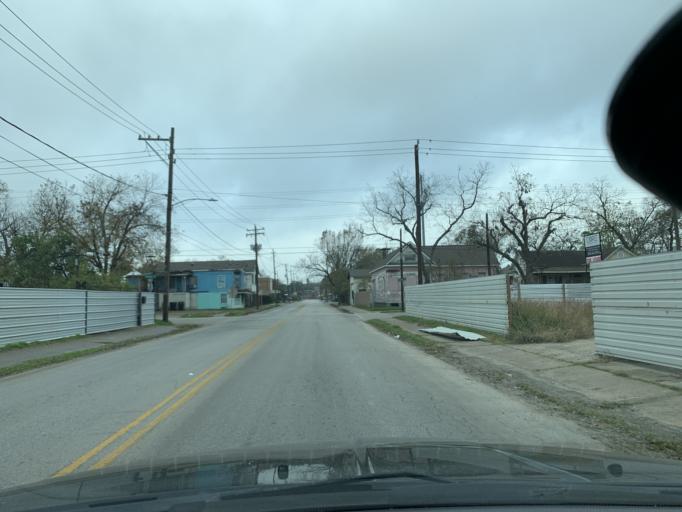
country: US
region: Texas
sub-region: Harris County
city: Houston
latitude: 29.7834
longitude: -95.3526
